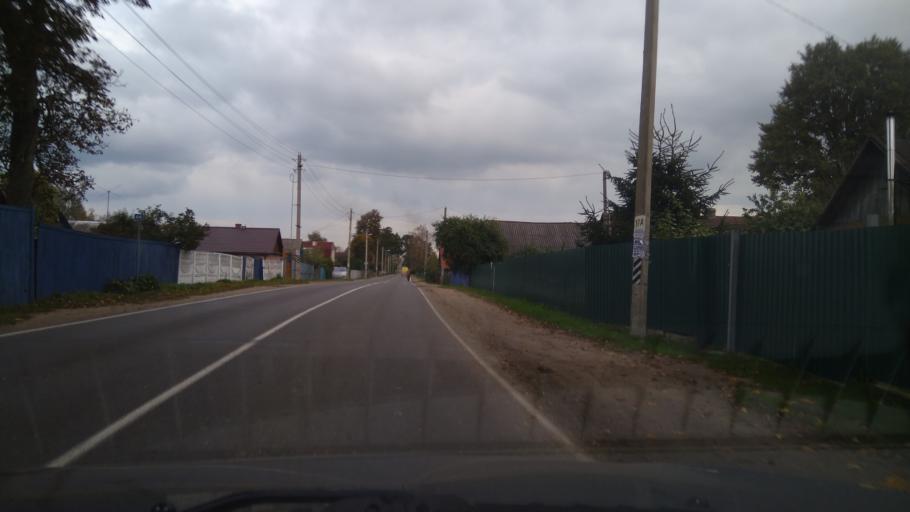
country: BY
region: Minsk
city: Dukora
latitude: 53.6701
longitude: 27.9395
